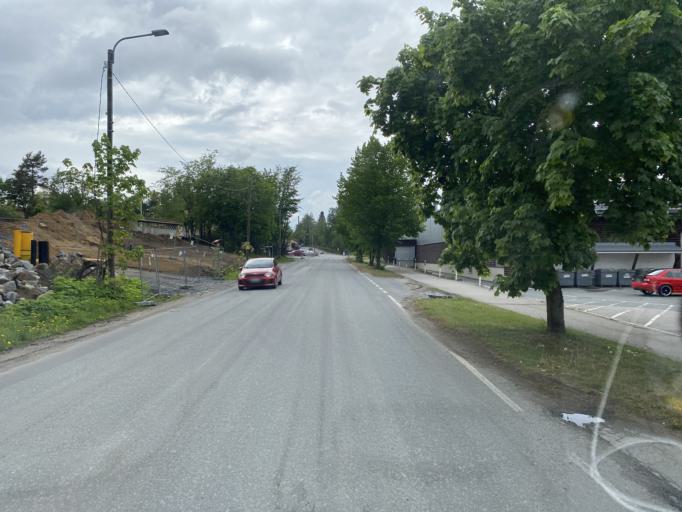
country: FI
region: Pirkanmaa
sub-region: Etelae-Pirkanmaa
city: Urjala
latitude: 61.0800
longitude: 23.5513
